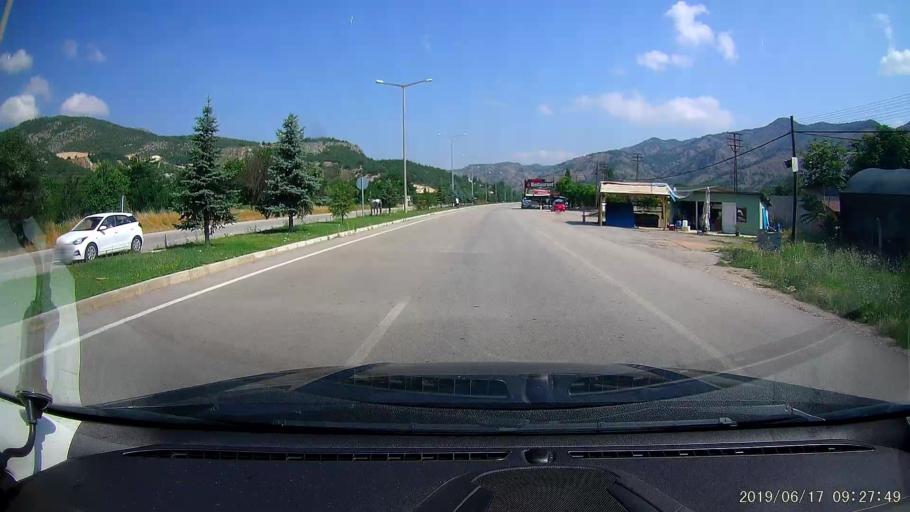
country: TR
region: Amasya
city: Amasya
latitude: 40.6813
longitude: 35.8241
